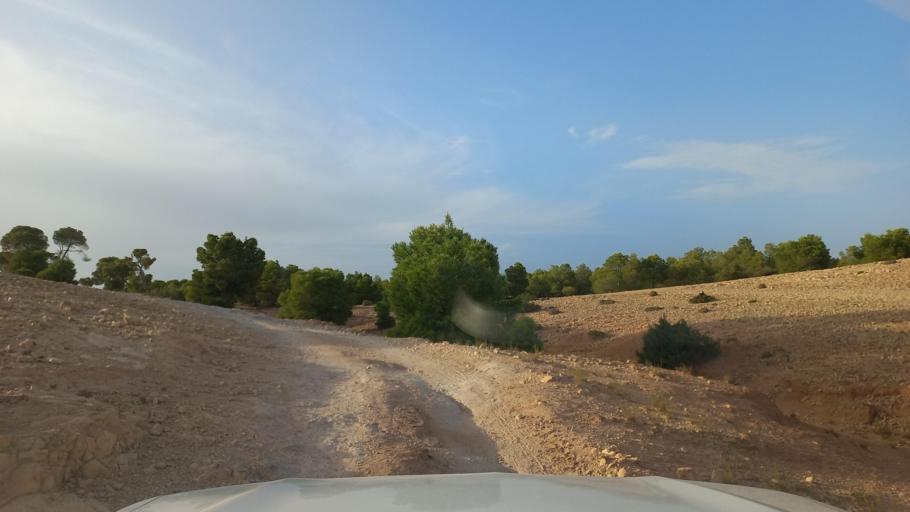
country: TN
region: Al Qasrayn
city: Sbiba
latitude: 35.4114
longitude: 8.8974
